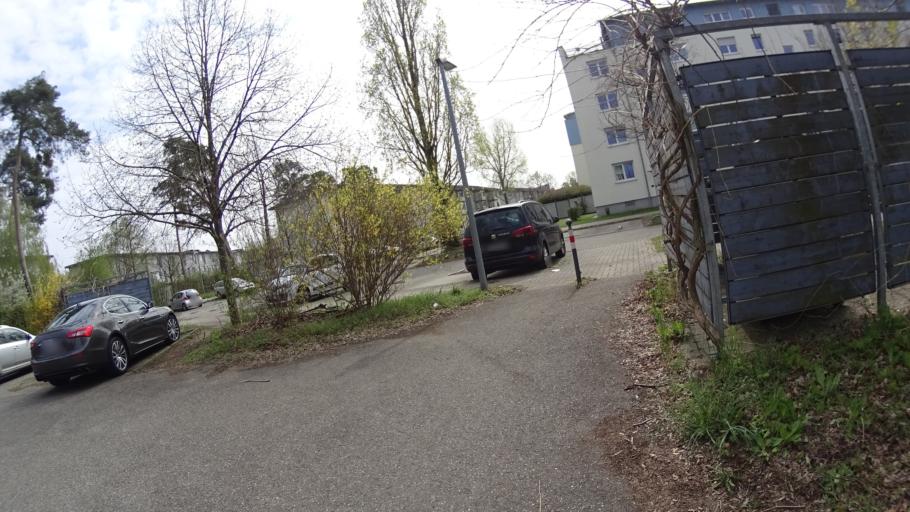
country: DE
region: Baden-Wuerttemberg
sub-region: Karlsruhe Region
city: Karlsruhe
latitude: 49.0320
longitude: 8.3884
